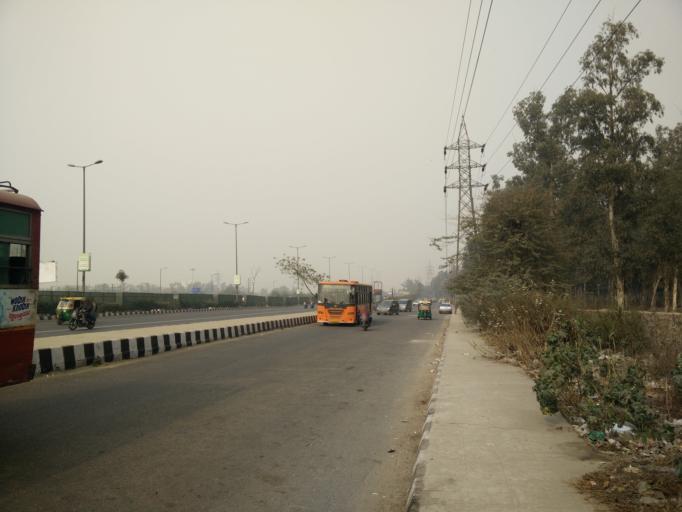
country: IN
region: Uttar Pradesh
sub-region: Gautam Buddha Nagar
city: Noida
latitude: 28.6487
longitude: 77.3187
